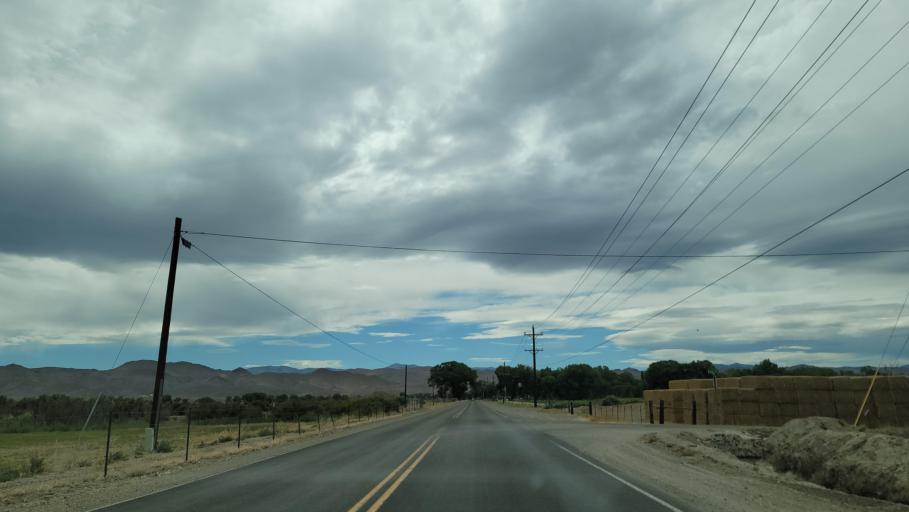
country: US
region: Nevada
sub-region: Lyon County
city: Yerington
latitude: 39.0481
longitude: -119.1719
